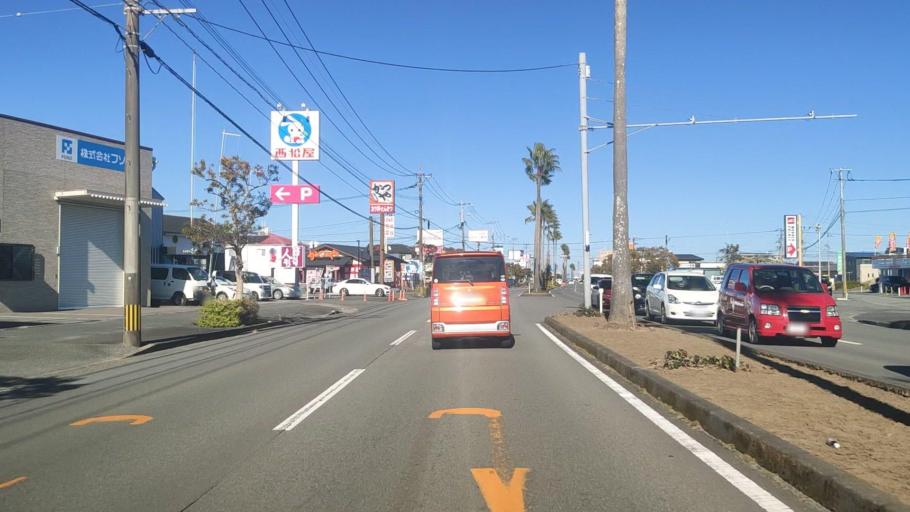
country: JP
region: Miyazaki
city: Miyazaki-shi
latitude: 31.9113
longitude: 131.4474
